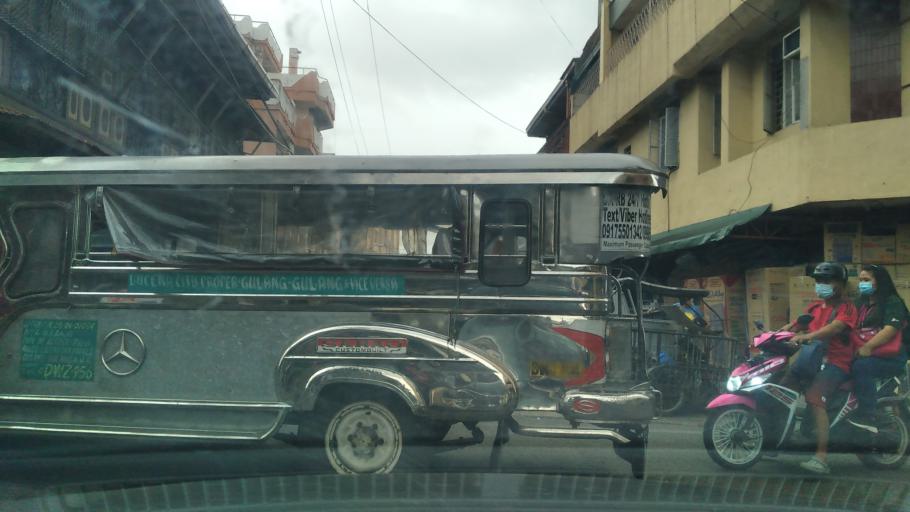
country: PH
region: Calabarzon
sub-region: Province of Quezon
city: Lucena
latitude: 13.9358
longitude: 121.6141
